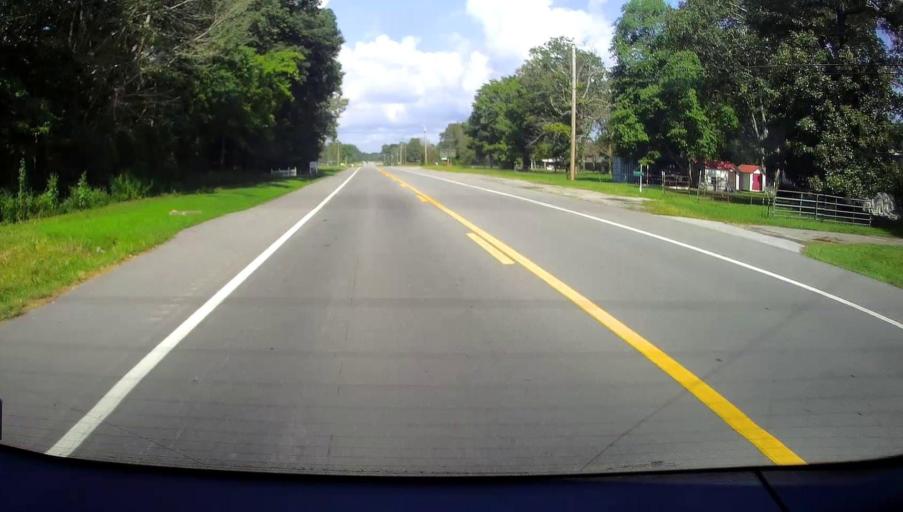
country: US
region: Tennessee
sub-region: Coffee County
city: Manchester
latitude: 35.5069
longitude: -86.1194
